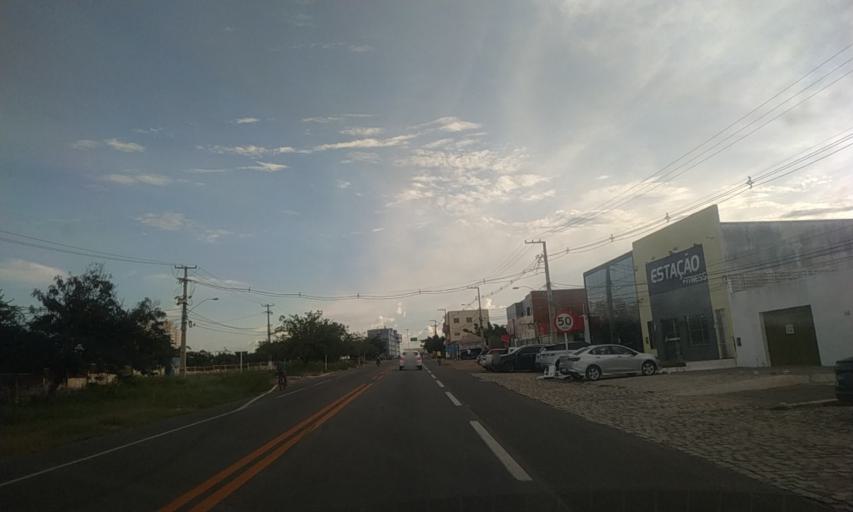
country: BR
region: Rio Grande do Norte
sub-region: Mossoro
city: Mossoro
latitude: -5.2076
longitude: -37.3314
